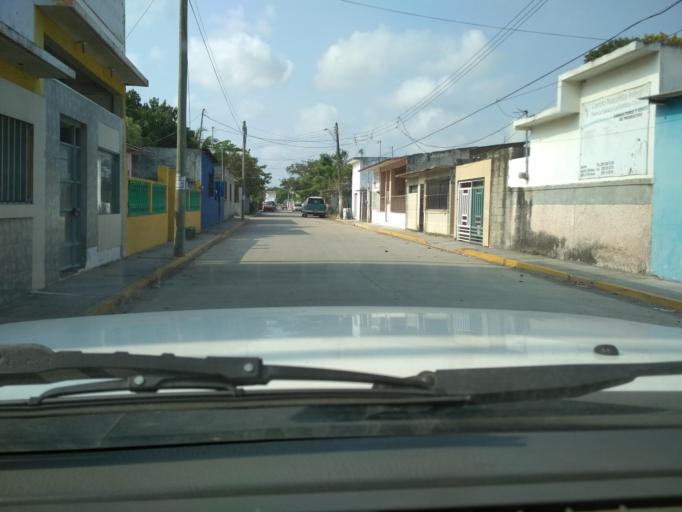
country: MX
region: Veracruz
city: El Tejar
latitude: 19.0822
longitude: -96.1599
